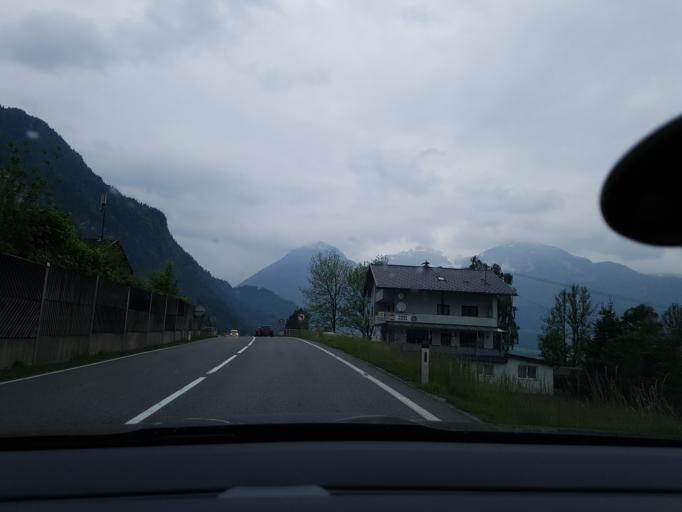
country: AT
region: Tyrol
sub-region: Politischer Bezirk Schwaz
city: Schlitters
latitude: 47.3778
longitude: 11.8422
